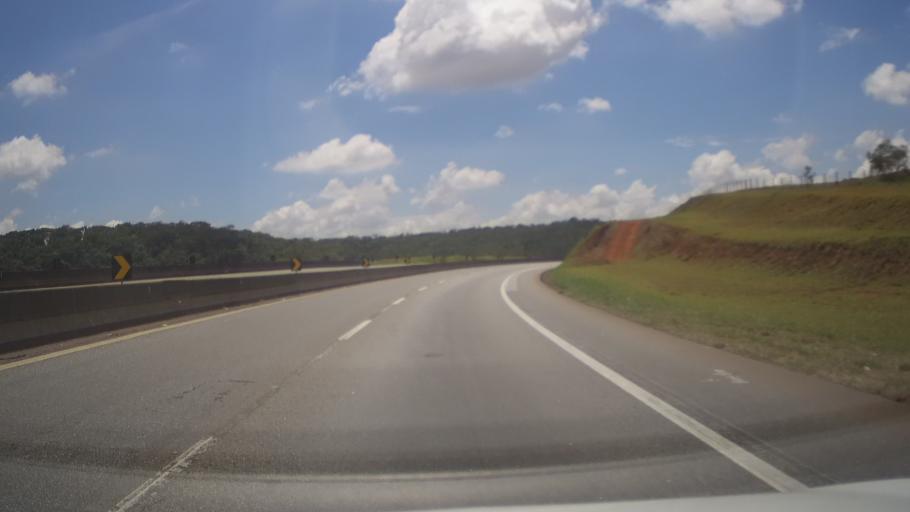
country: BR
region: Minas Gerais
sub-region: Sao Goncalo Do Sapucai
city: Sao Goncalo do Sapucai
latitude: -21.9213
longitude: -45.6112
